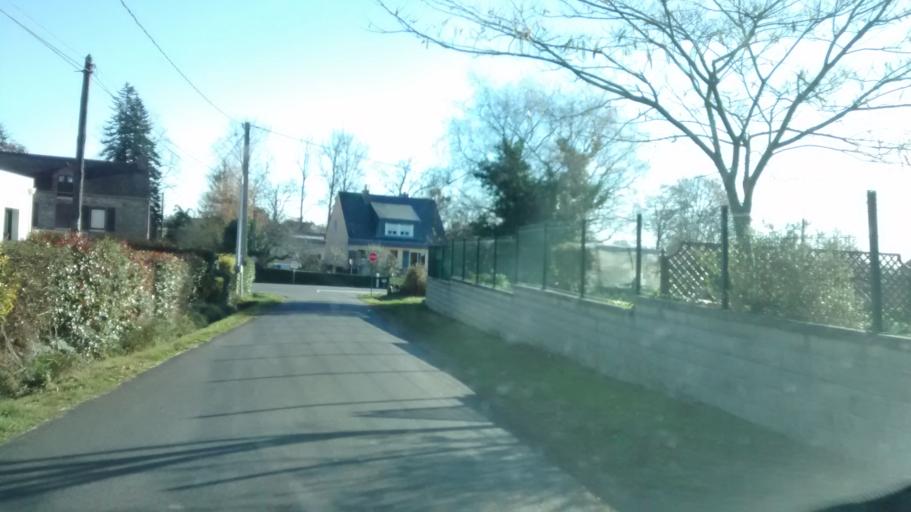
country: FR
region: Brittany
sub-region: Departement d'Ille-et-Vilaine
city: Liffre
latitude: 48.2039
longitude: -1.5109
